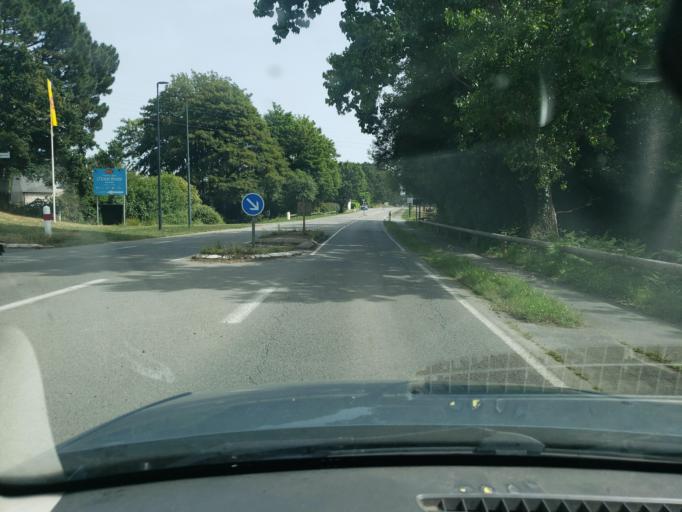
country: FR
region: Brittany
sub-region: Departement du Finistere
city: Plobannalec-Lesconil
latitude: 47.8127
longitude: -4.2270
